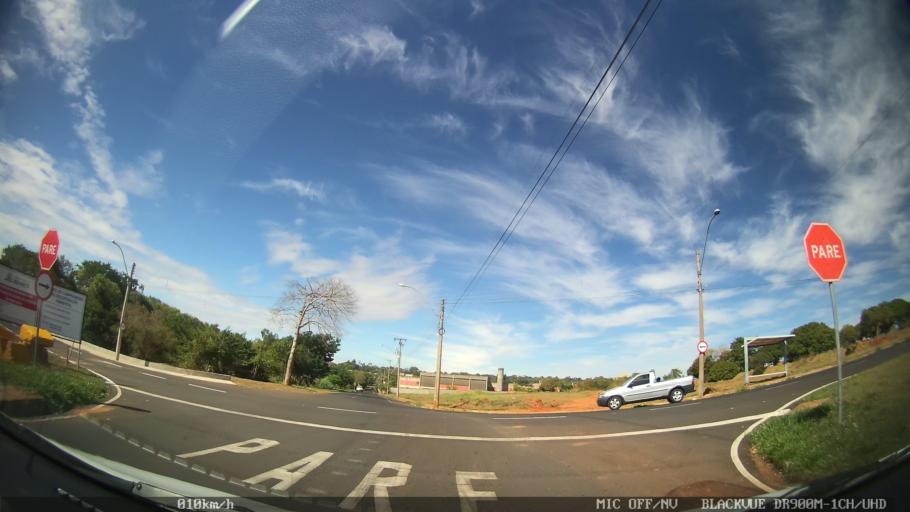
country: BR
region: Sao Paulo
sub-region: Sao Jose Do Rio Preto
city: Sao Jose do Rio Preto
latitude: -20.8430
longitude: -49.3622
